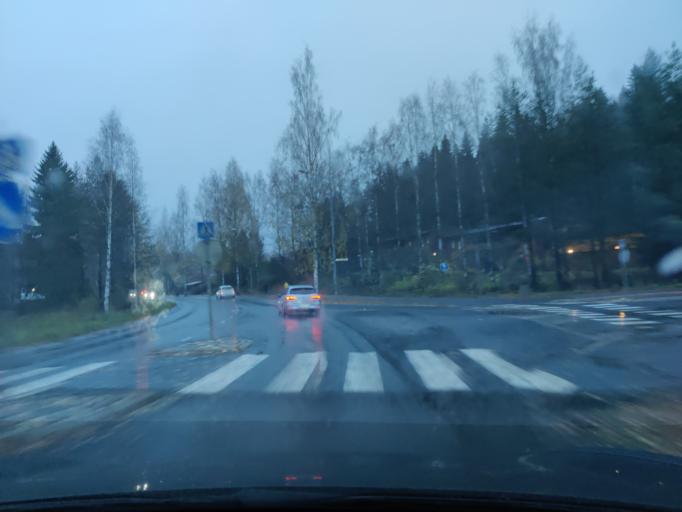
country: FI
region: Northern Savo
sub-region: Kuopio
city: Kuopio
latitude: 62.8511
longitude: 27.6410
